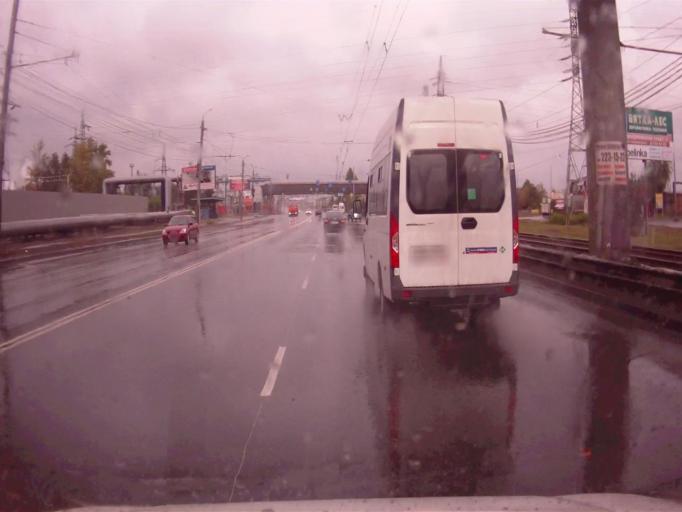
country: RU
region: Chelyabinsk
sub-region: Gorod Chelyabinsk
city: Chelyabinsk
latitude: 55.2035
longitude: 61.3853
